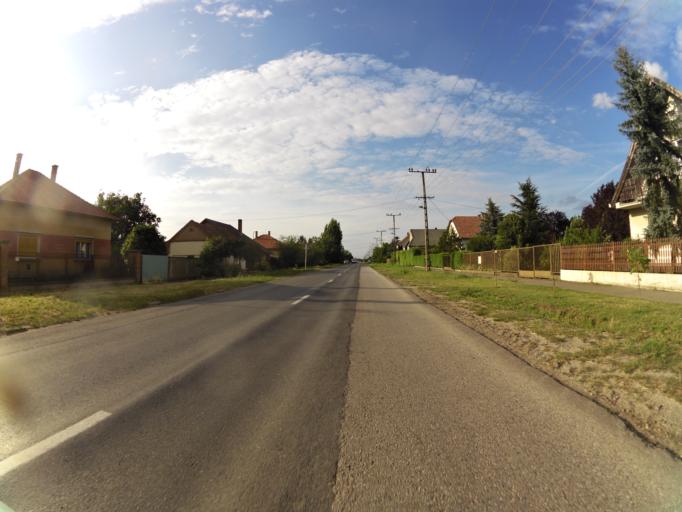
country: HU
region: Csongrad
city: Sandorfalva
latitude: 46.3610
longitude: 20.1138
